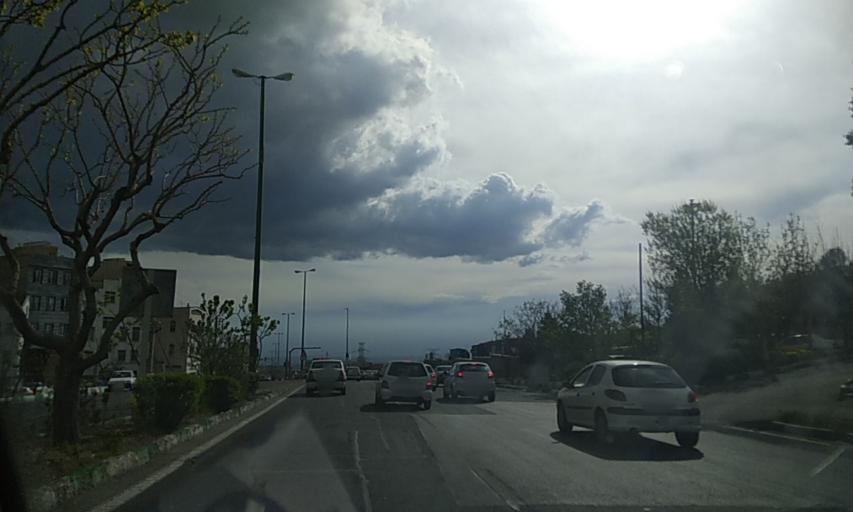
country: IR
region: Tehran
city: Tajrish
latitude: 35.7778
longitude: 51.3041
